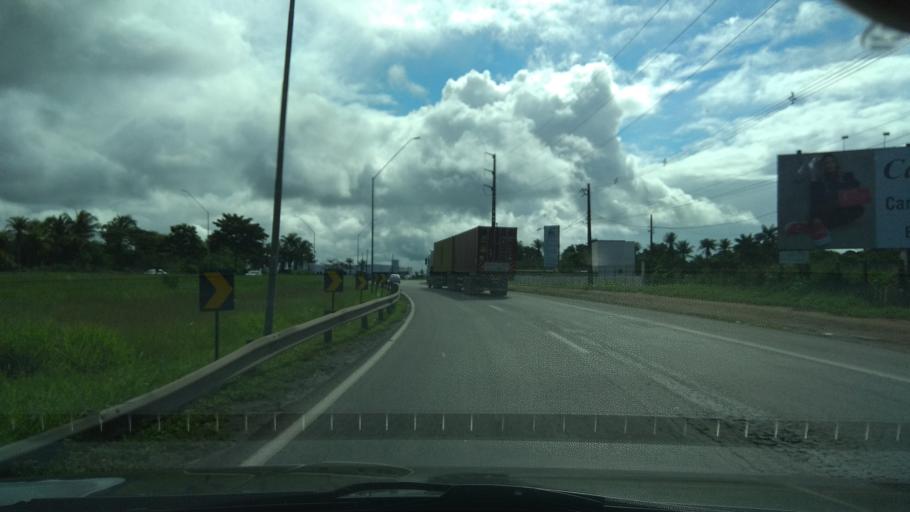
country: BR
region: Bahia
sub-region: Conceicao Do Jacuipe
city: Conceicao do Jacuipe
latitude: -12.3766
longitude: -38.8033
